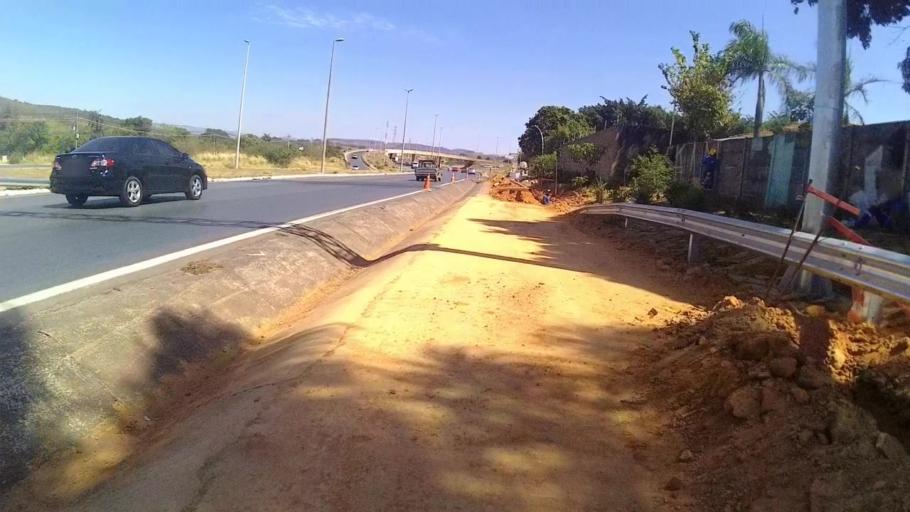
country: BR
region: Federal District
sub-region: Brasilia
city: Brasilia
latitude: -15.6440
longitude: -47.8478
